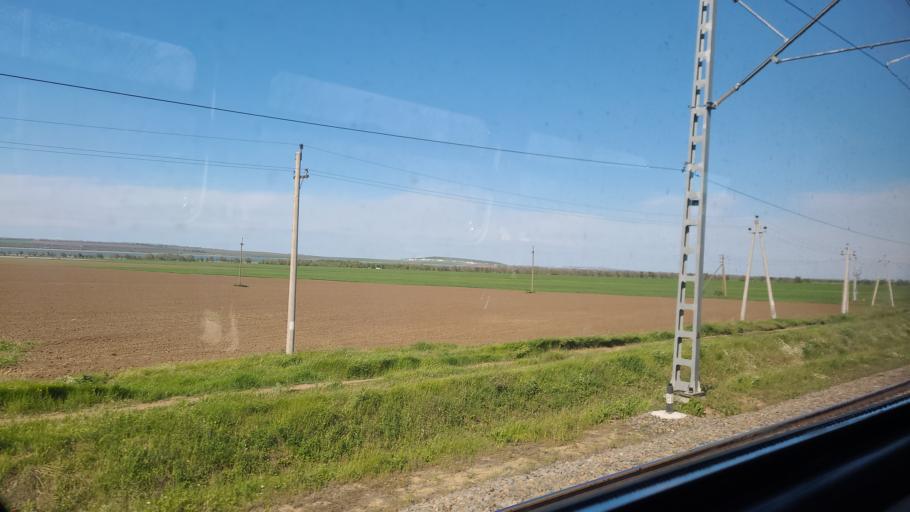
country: RU
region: Krasnodarskiy
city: Starotitarovskaya
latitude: 45.1980
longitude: 37.2021
